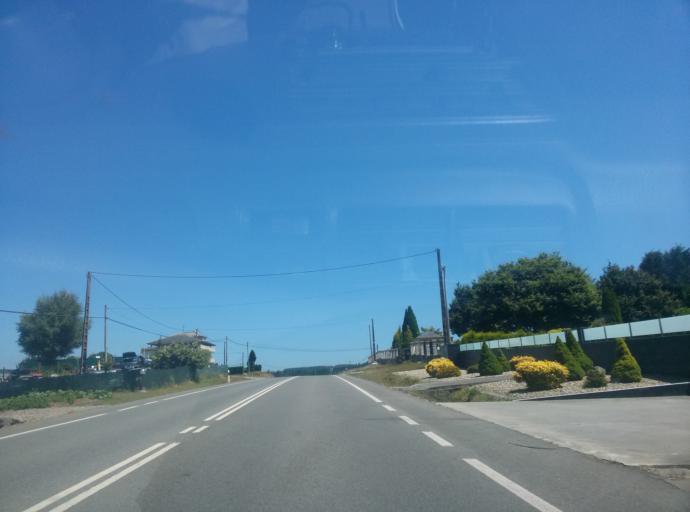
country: ES
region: Galicia
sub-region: Provincia de Lugo
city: Castro de Rei
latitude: 43.2359
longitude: -7.4008
